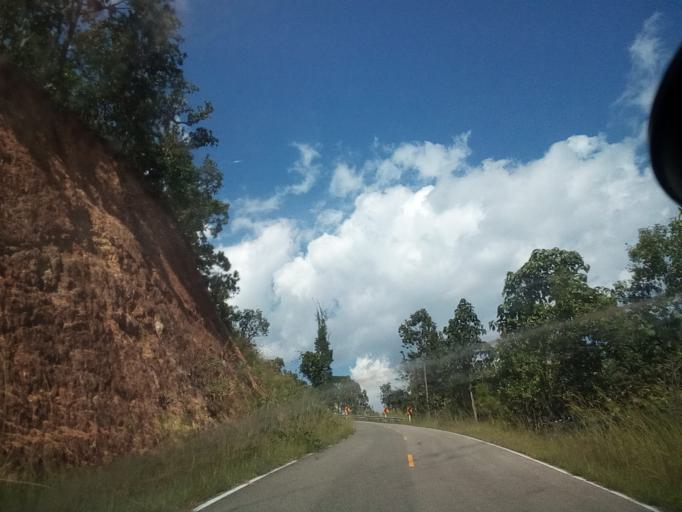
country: TH
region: Chiang Mai
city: Samoeng
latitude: 18.8673
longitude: 98.6934
